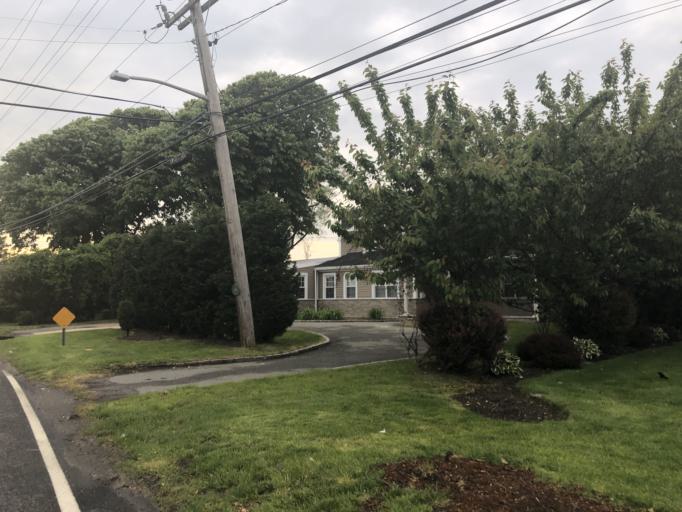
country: US
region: New York
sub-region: Nassau County
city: Atlantic Beach
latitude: 40.5885
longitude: -73.7201
